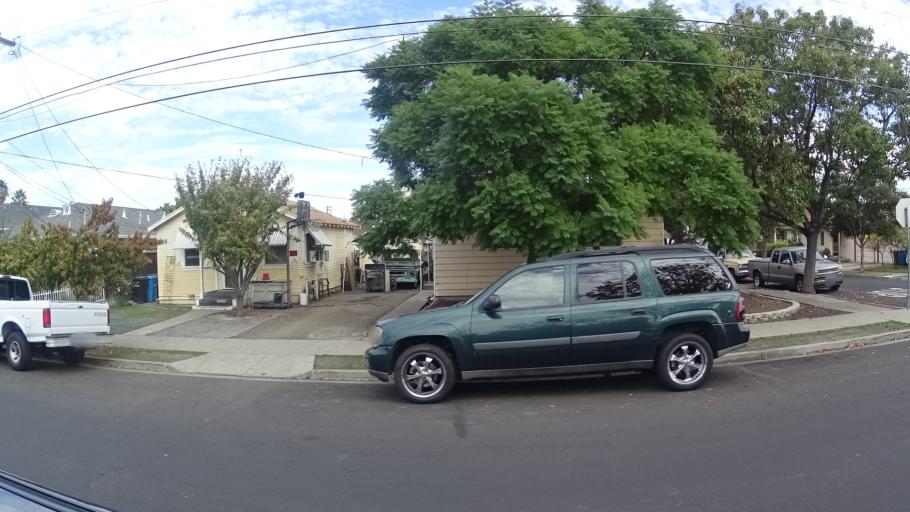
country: US
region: California
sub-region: Santa Clara County
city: Santa Clara
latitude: 37.3556
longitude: -121.9479
